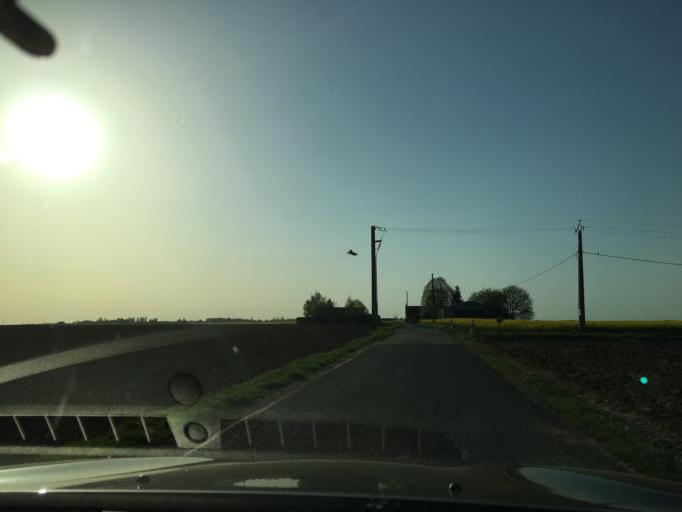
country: FR
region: Centre
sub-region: Departement du Loir-et-Cher
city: Ouzouer-le-Marche
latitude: 47.9041
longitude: 1.5613
